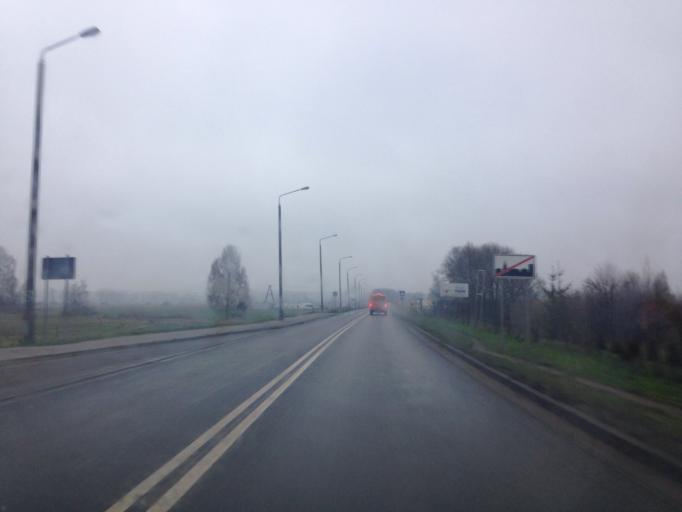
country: PL
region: Kujawsko-Pomorskie
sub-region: Powiat nakielski
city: Naklo nad Notecia
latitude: 53.1196
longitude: 17.6033
